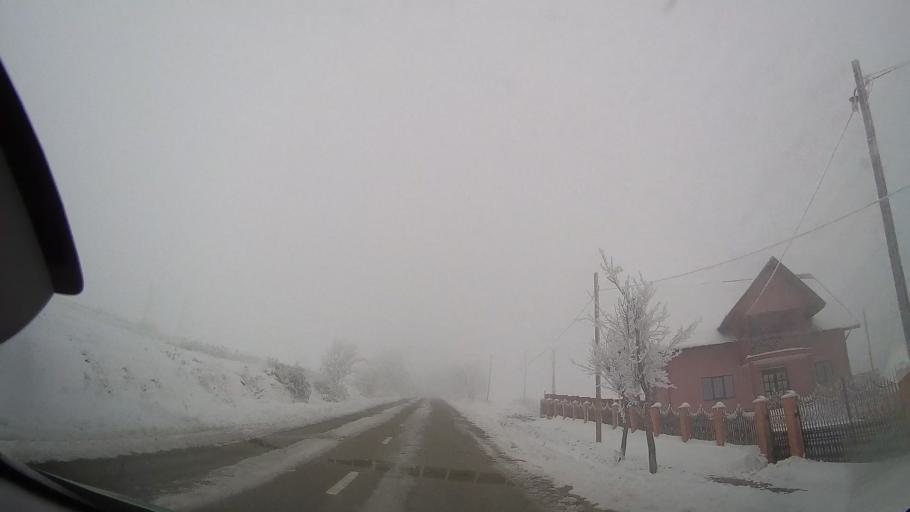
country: RO
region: Neamt
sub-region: Comuna Valea Ursului
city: Valea Ursului
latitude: 46.8010
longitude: 27.0751
